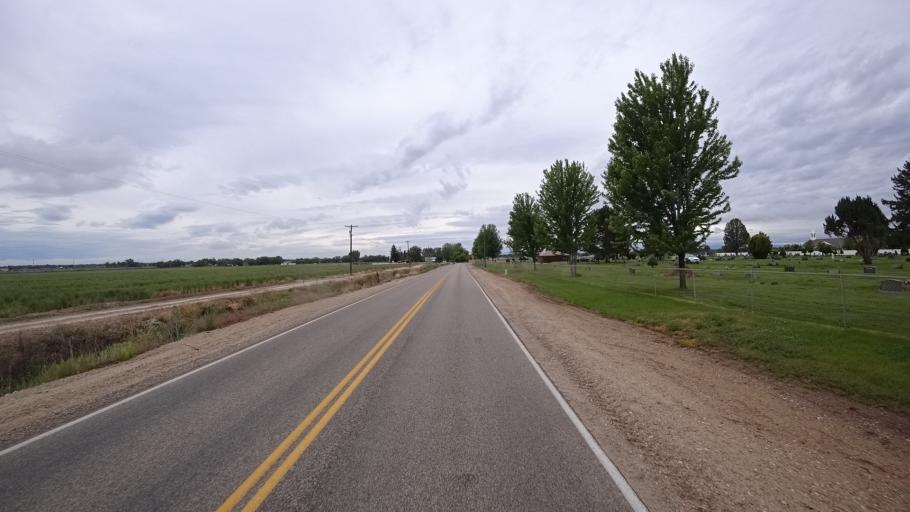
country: US
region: Idaho
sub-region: Ada County
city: Star
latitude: 43.7083
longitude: -116.4685
